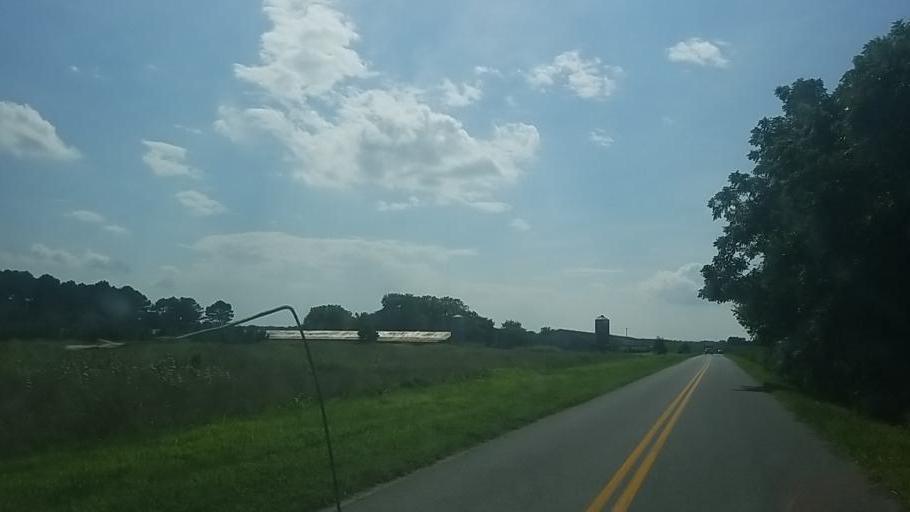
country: US
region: Maryland
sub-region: Somerset County
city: Princess Anne
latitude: 38.2614
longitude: -75.6785
